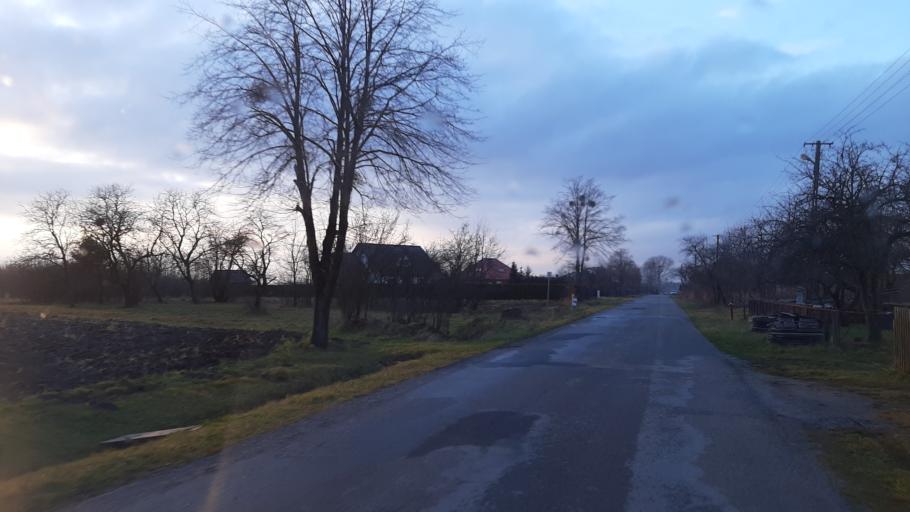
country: PL
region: Lublin Voivodeship
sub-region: Powiat lubelski
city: Garbow
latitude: 51.3805
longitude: 22.3973
